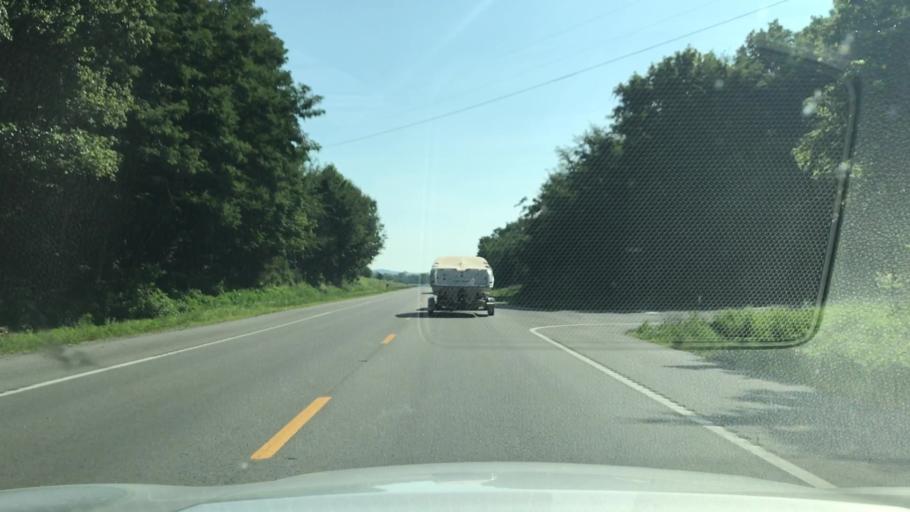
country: US
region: Tennessee
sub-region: Pickett County
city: Byrdstown
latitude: 36.6122
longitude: -85.1003
